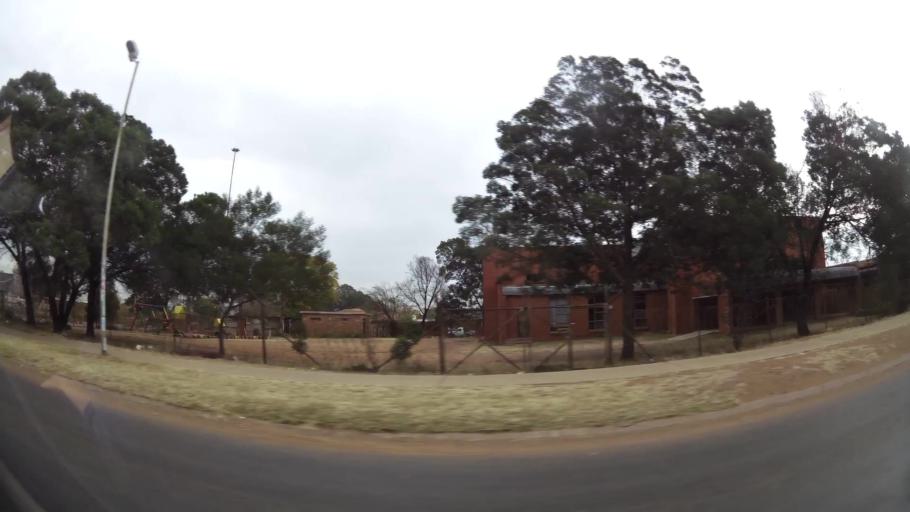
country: ZA
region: Gauteng
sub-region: City of Tshwane Metropolitan Municipality
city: Pretoria
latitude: -25.7122
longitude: 28.3301
